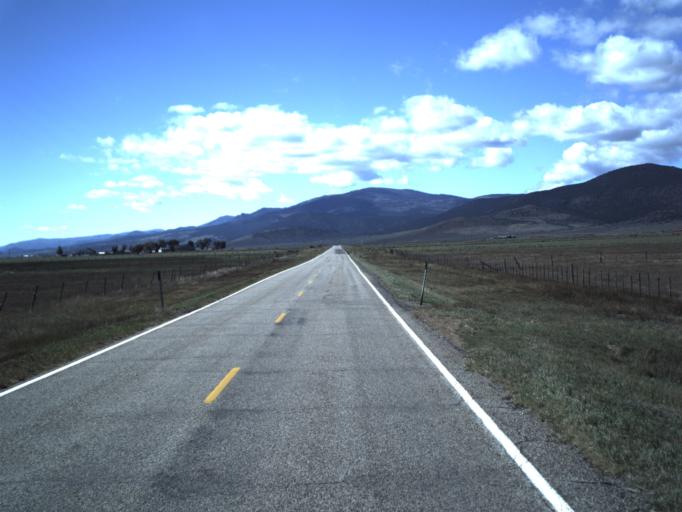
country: US
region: Utah
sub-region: Wayne County
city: Loa
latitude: 38.4875
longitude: -111.8864
